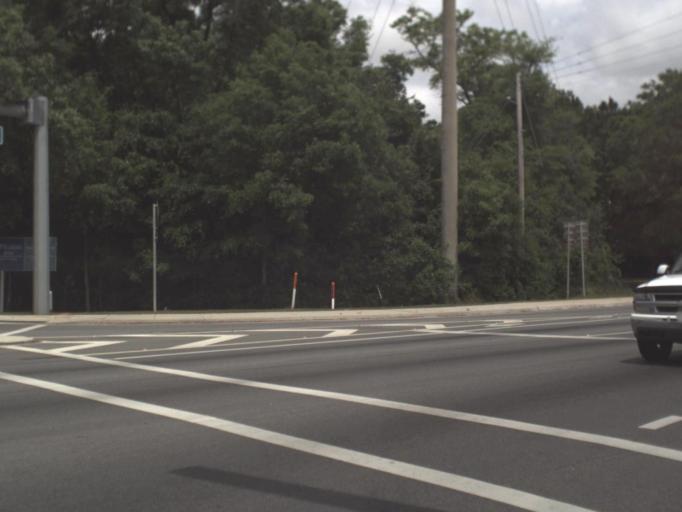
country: US
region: Florida
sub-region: Santa Rosa County
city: Bagdad
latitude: 30.6023
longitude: -87.0736
